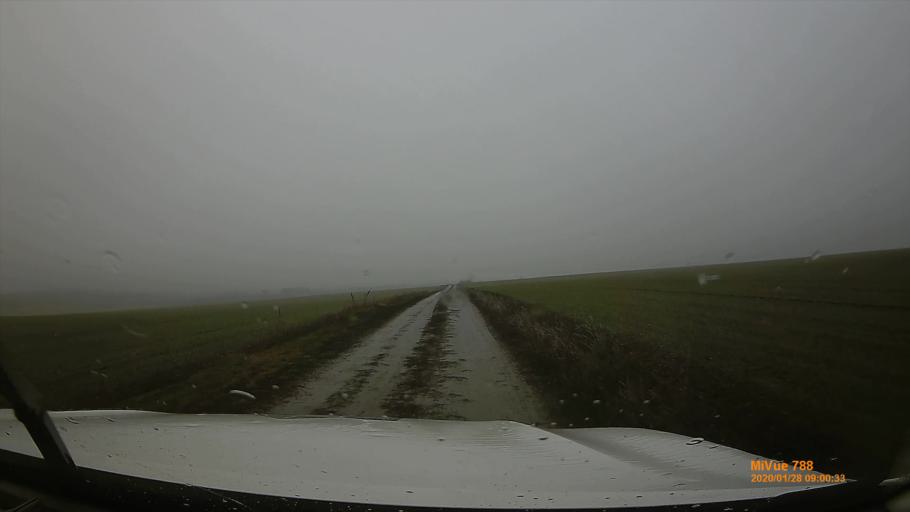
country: HU
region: Pest
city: Pilis
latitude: 47.3114
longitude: 19.5463
